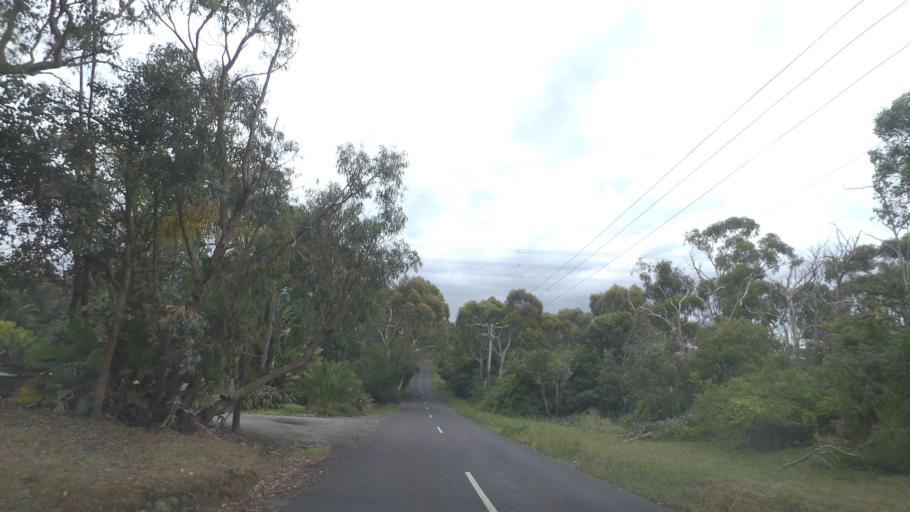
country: AU
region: Victoria
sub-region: Manningham
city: Warrandyte
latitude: -37.7652
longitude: 145.2338
